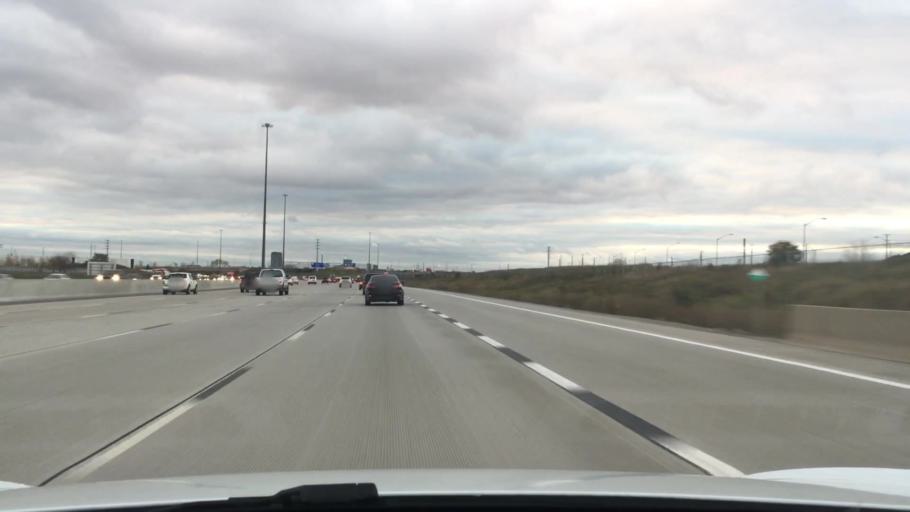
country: CA
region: Ontario
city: Concord
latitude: 43.8238
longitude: -79.4682
